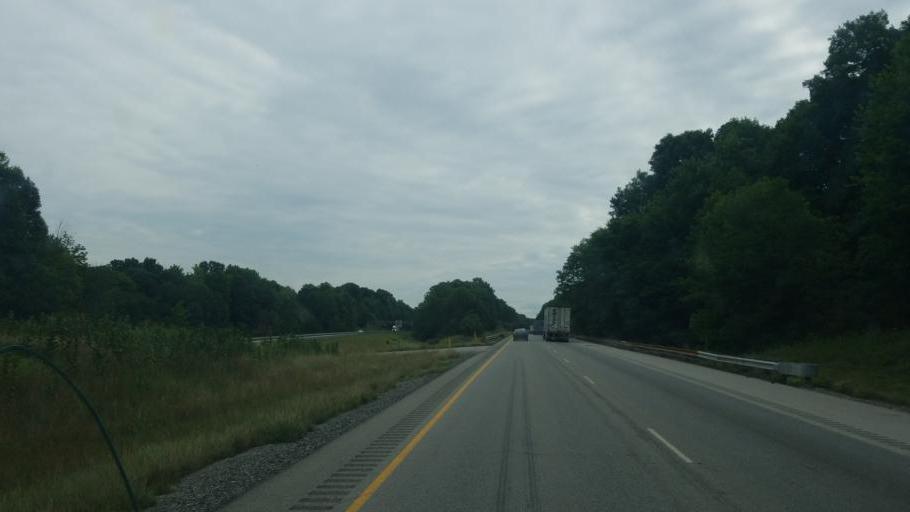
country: US
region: Indiana
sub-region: Putnam County
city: Cloverdale
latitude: 39.5162
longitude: -86.9122
